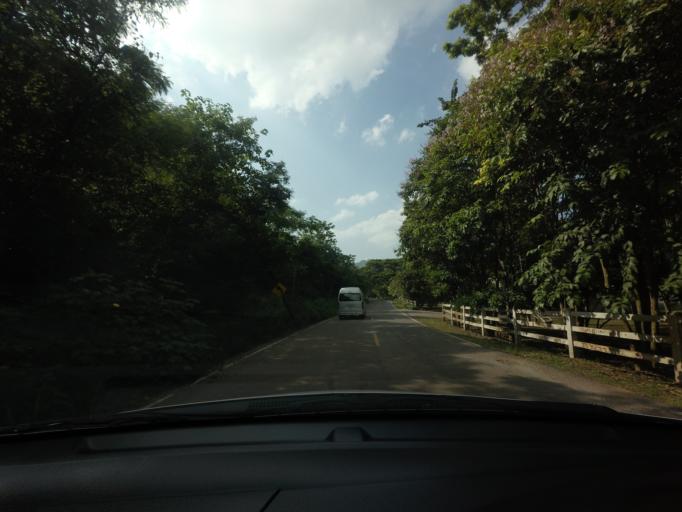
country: TH
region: Nakhon Ratchasima
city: Pak Chong
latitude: 14.5286
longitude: 101.3946
